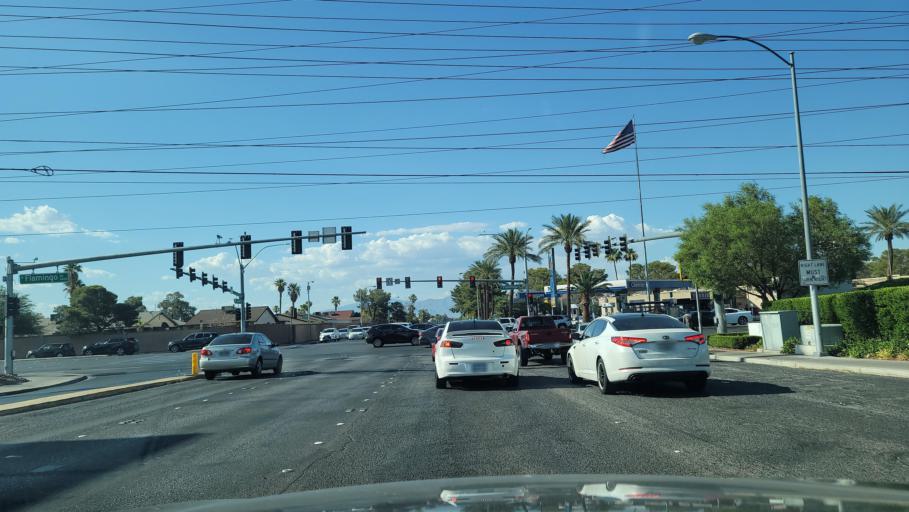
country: US
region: Nevada
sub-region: Clark County
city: Spring Valley
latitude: 36.1150
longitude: -115.1994
